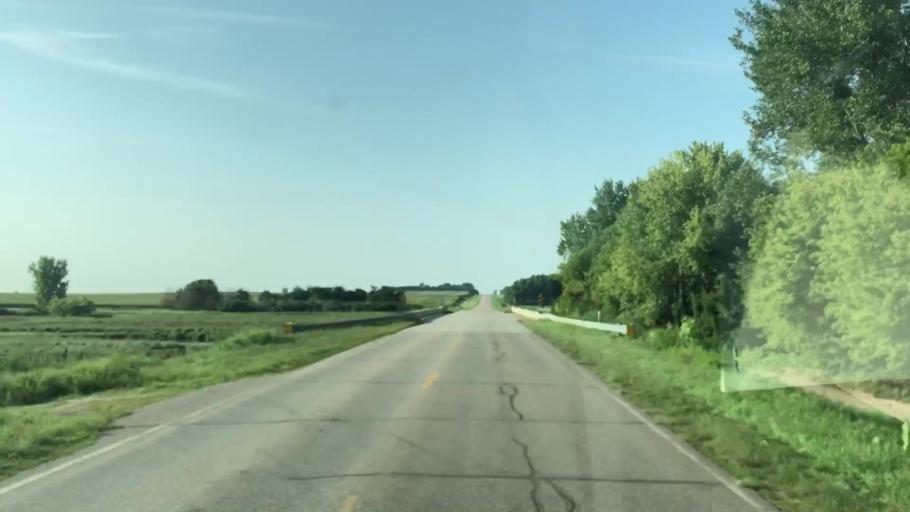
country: US
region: Iowa
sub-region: Lyon County
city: George
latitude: 43.3340
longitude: -95.9987
